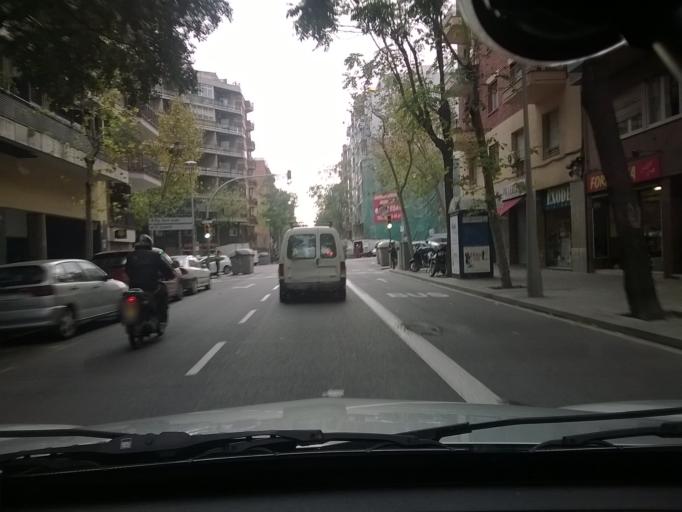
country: ES
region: Catalonia
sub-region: Provincia de Barcelona
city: Horta-Guinardo
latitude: 41.4091
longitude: 2.1715
